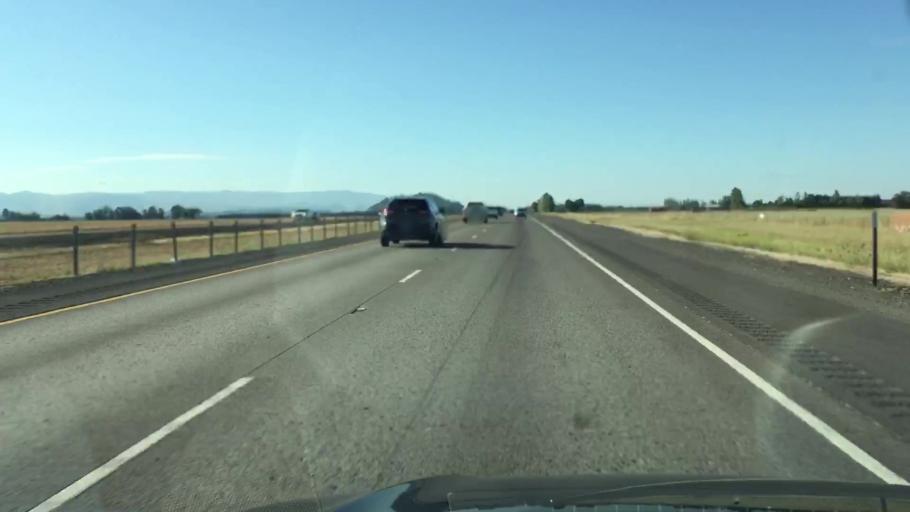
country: US
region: Oregon
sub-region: Linn County
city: Tangent
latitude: 44.5032
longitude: -123.0620
